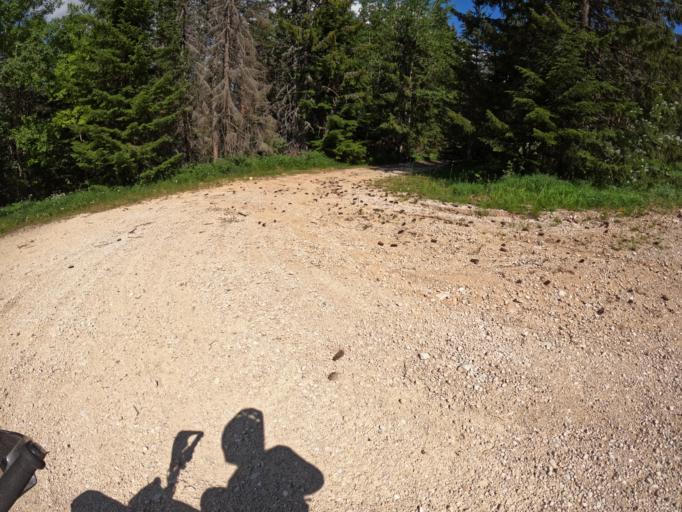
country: BA
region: Federation of Bosnia and Herzegovina
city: Glamoc
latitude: 44.0110
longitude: 17.0040
